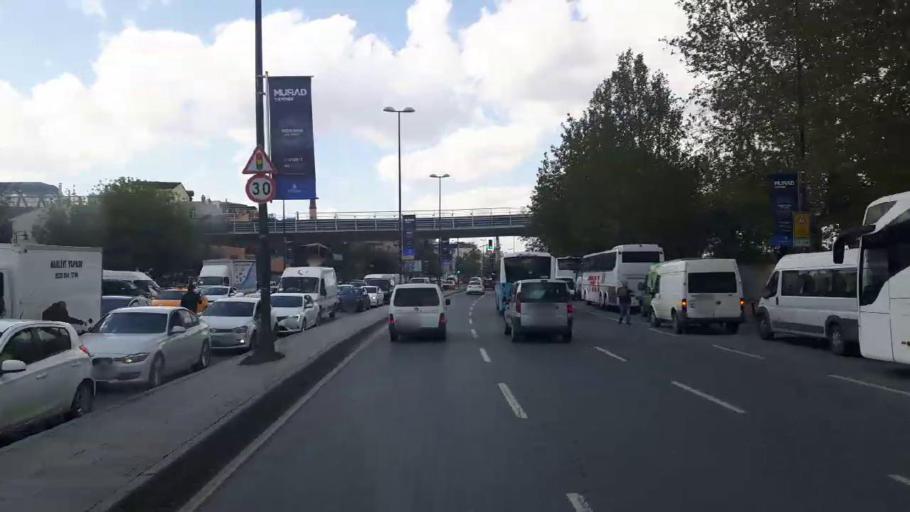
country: TR
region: Istanbul
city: Eminoenue
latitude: 41.0195
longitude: 28.9652
